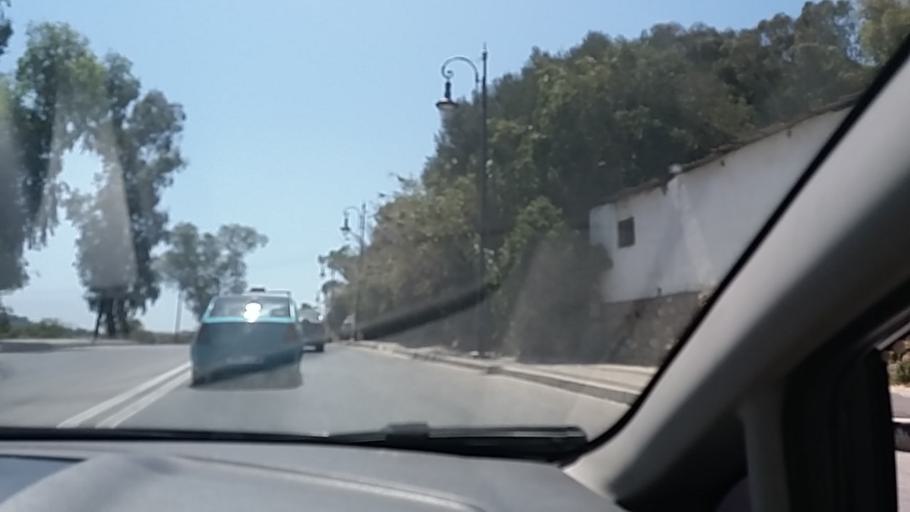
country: MA
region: Tanger-Tetouan
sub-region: Tanger-Assilah
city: Tangier
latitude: 35.7861
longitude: -5.8369
